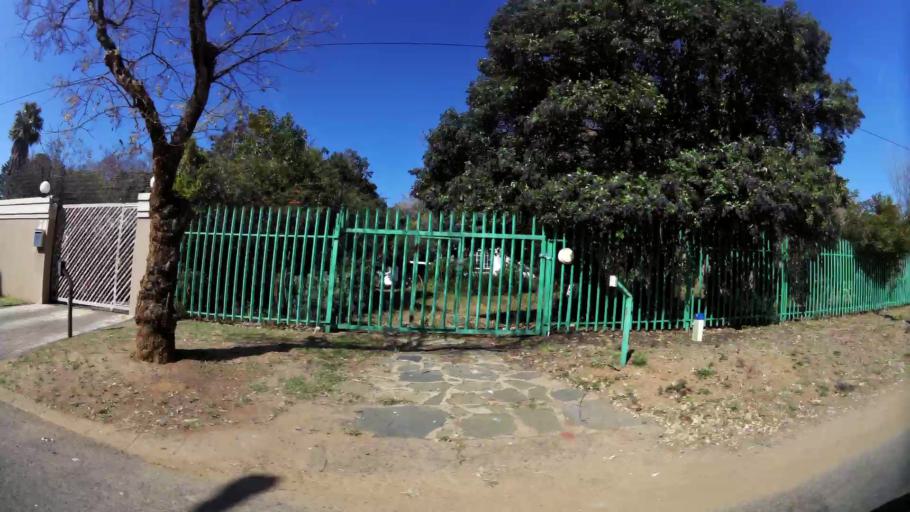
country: ZA
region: Gauteng
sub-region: City of Johannesburg Metropolitan Municipality
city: Modderfontein
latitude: -26.1371
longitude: 28.1054
